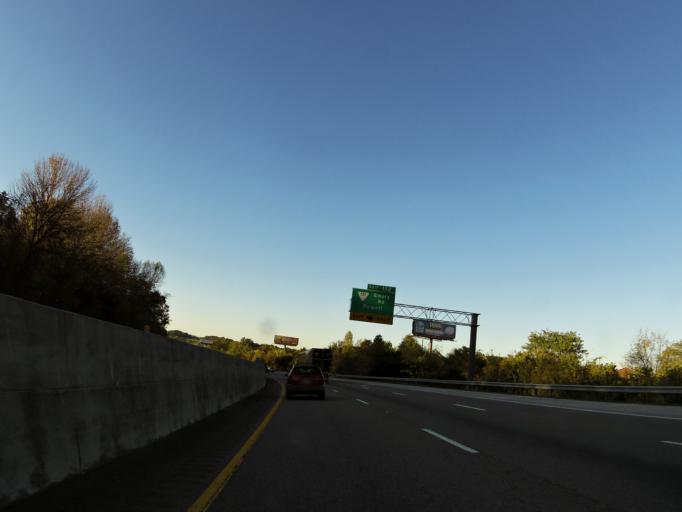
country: US
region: Tennessee
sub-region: Knox County
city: Knoxville
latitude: 36.0387
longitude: -83.9962
